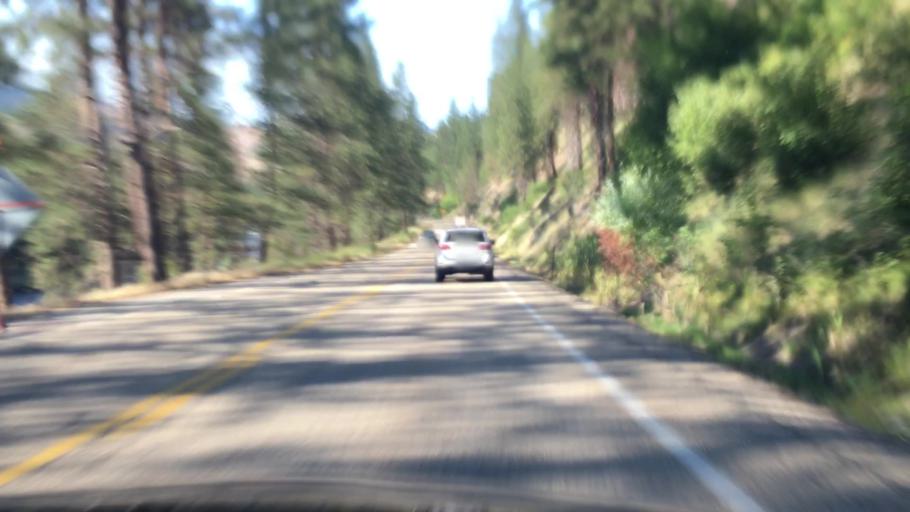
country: US
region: Idaho
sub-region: Boise County
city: Idaho City
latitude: 44.0628
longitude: -116.1222
